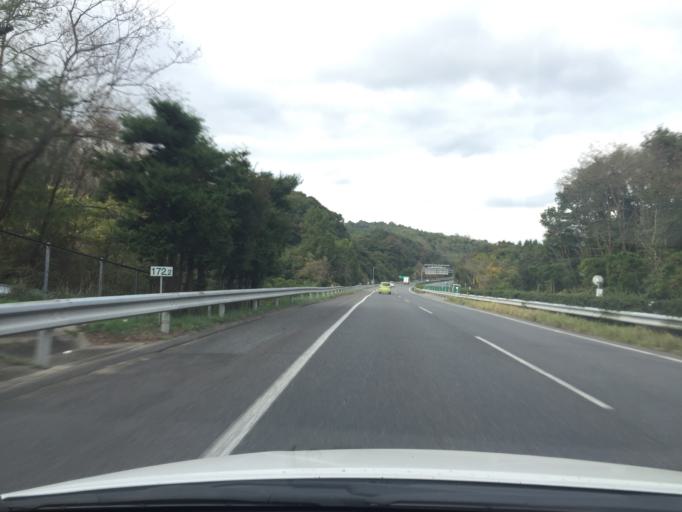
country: JP
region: Fukushima
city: Iwaki
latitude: 37.0457
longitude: 140.8208
